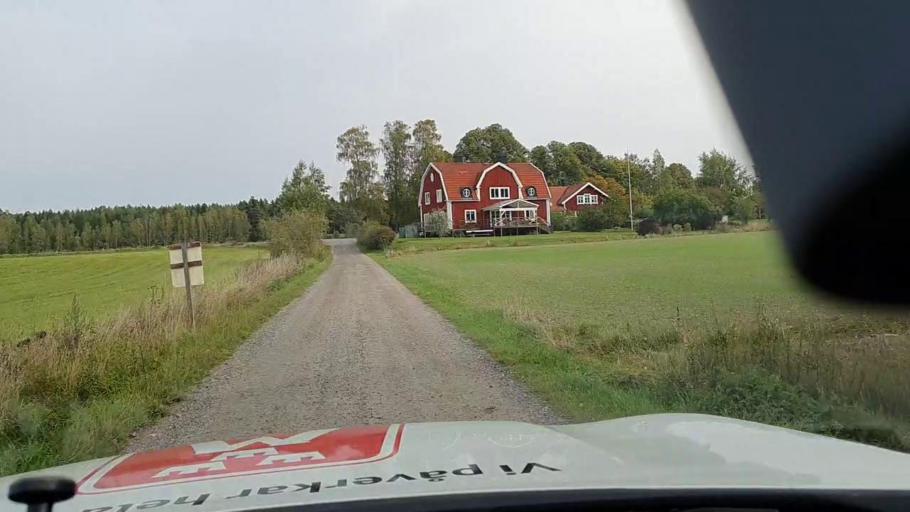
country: SE
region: Soedermanland
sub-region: Nykopings Kommun
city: Stigtomta
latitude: 58.7903
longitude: 16.7450
